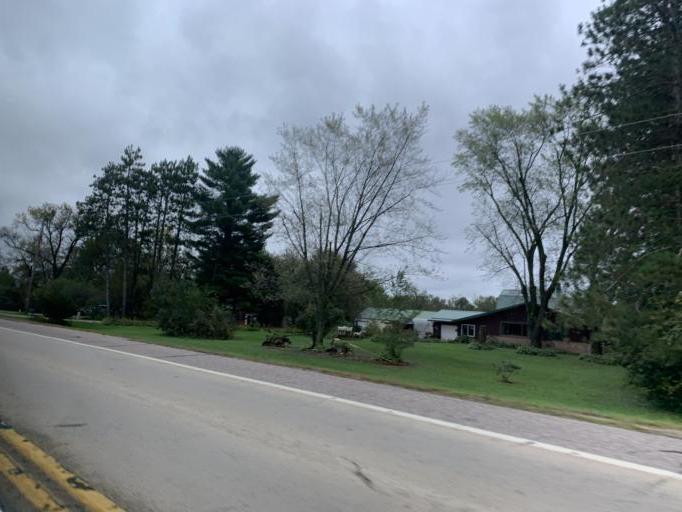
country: US
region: Wisconsin
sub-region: Sauk County
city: Sauk City
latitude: 43.2607
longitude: -89.8025
